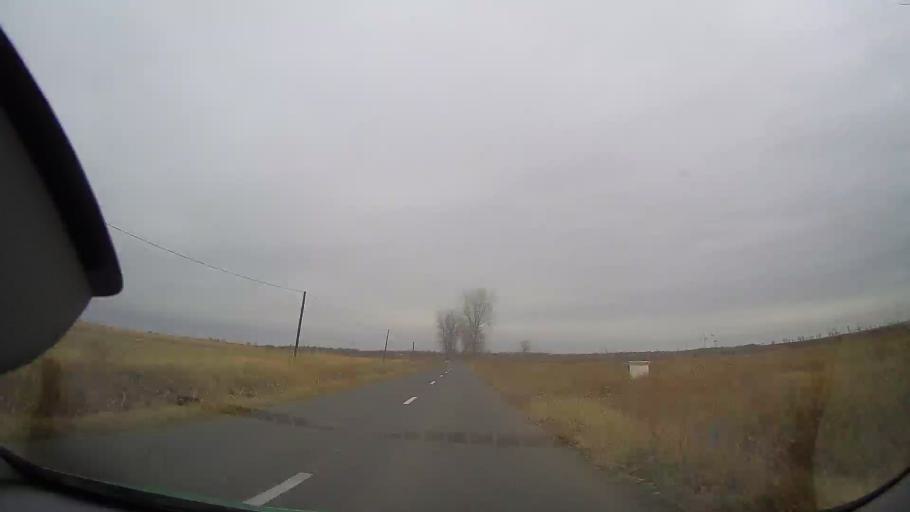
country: RO
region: Braila
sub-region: Comuna Budesti
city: Tataru
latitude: 44.8371
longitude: 27.4167
